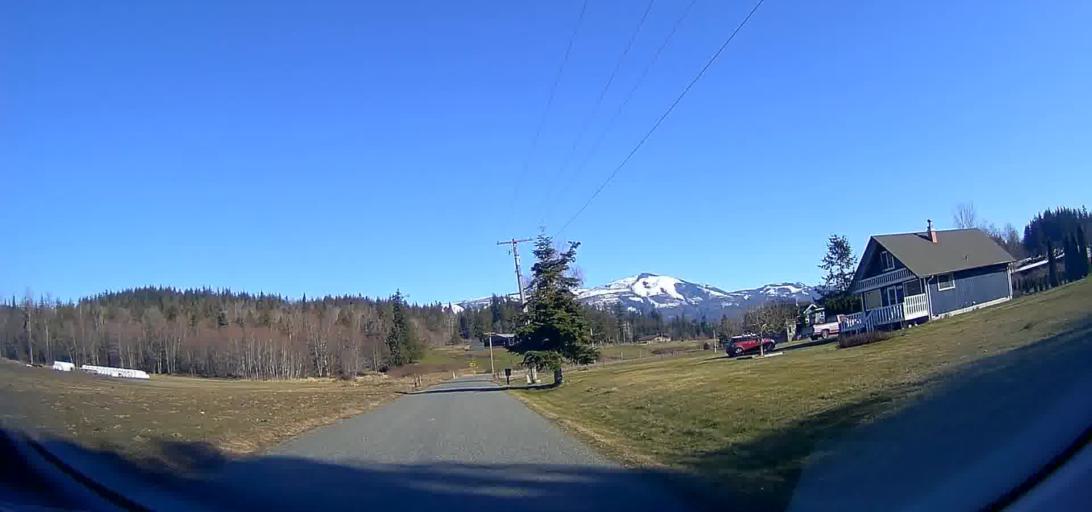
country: US
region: Washington
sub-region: Skagit County
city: Clear Lake
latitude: 48.4497
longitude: -122.2606
